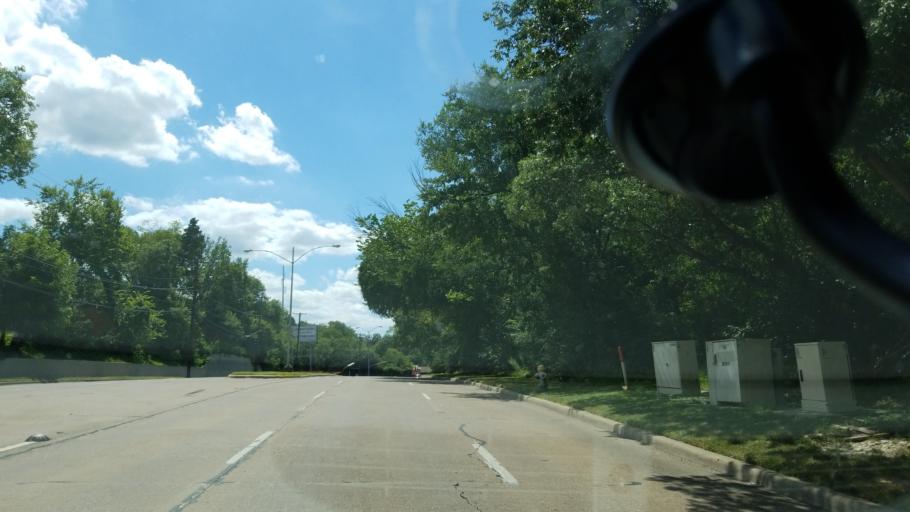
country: US
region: Texas
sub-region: Dallas County
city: Cockrell Hill
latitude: 32.7050
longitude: -96.8719
